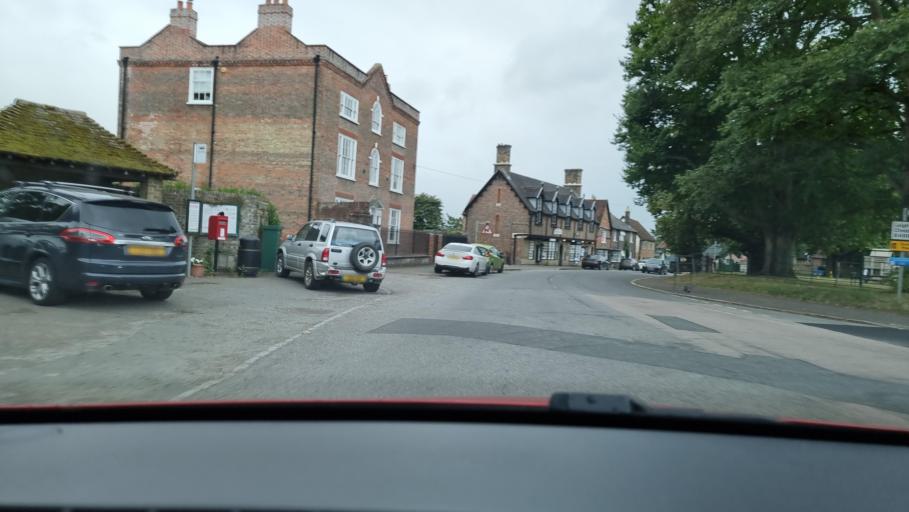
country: GB
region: England
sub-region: Buckinghamshire
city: Ivinghoe
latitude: 51.8362
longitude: -0.6296
